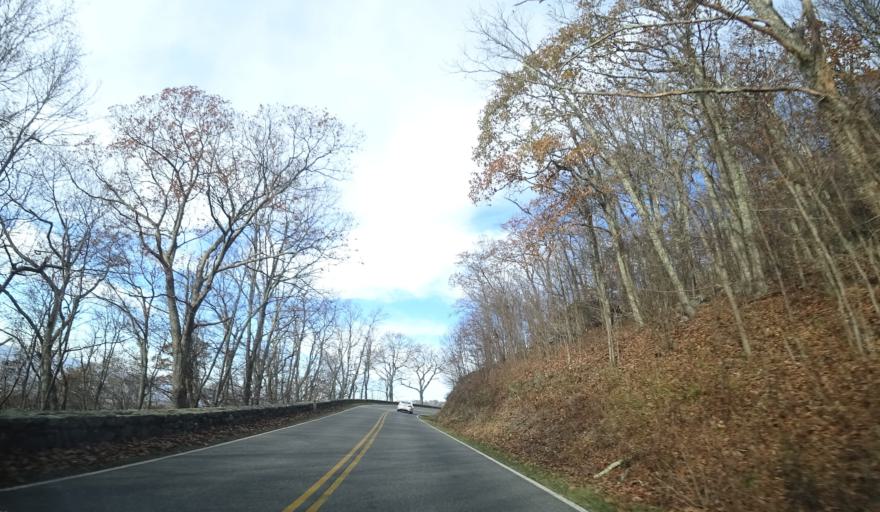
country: US
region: Virginia
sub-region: Rockingham County
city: Elkton
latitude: 38.3699
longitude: -78.5308
